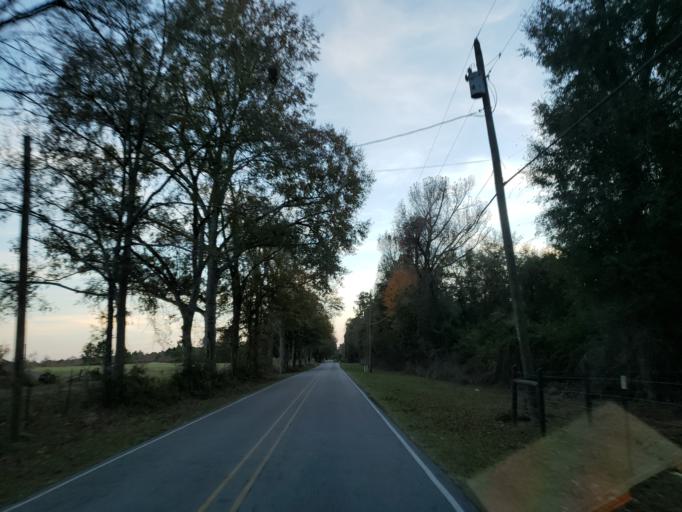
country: US
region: Mississippi
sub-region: Forrest County
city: Hattiesburg
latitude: 31.2482
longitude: -89.3140
